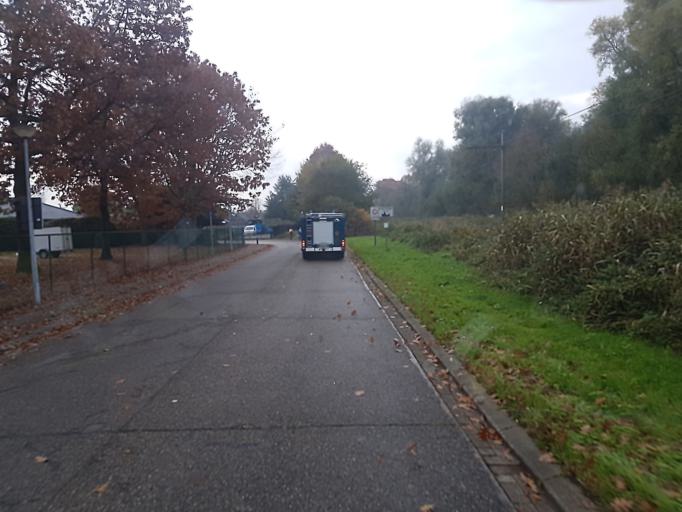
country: BE
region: Flanders
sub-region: Provincie Antwerpen
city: Turnhout
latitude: 51.3111
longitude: 4.9321
